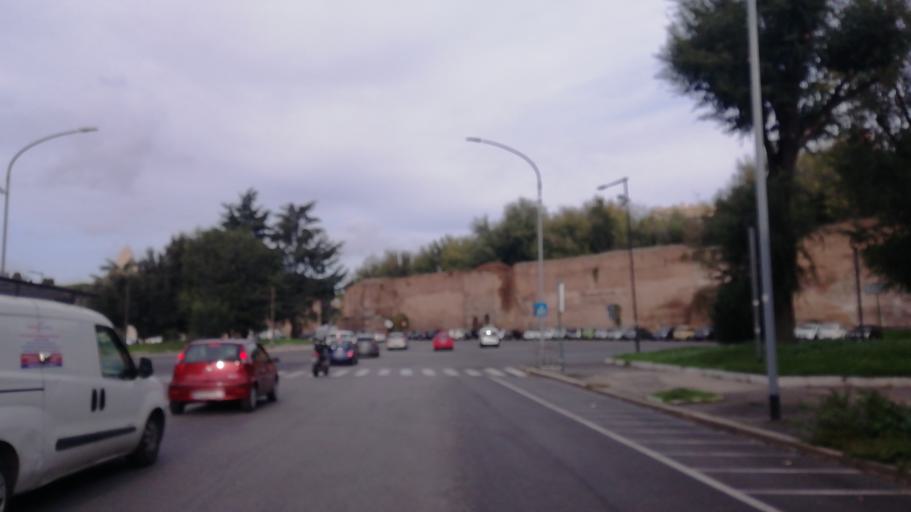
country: IT
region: Latium
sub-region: Citta metropolitana di Roma Capitale
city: Rome
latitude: 41.8758
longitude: 12.4838
